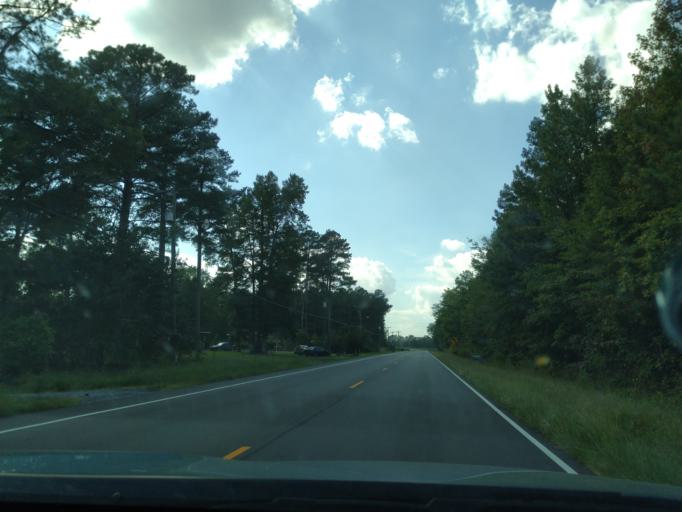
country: US
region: North Carolina
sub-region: Pitt County
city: Bethel
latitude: 35.8248
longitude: -77.3219
